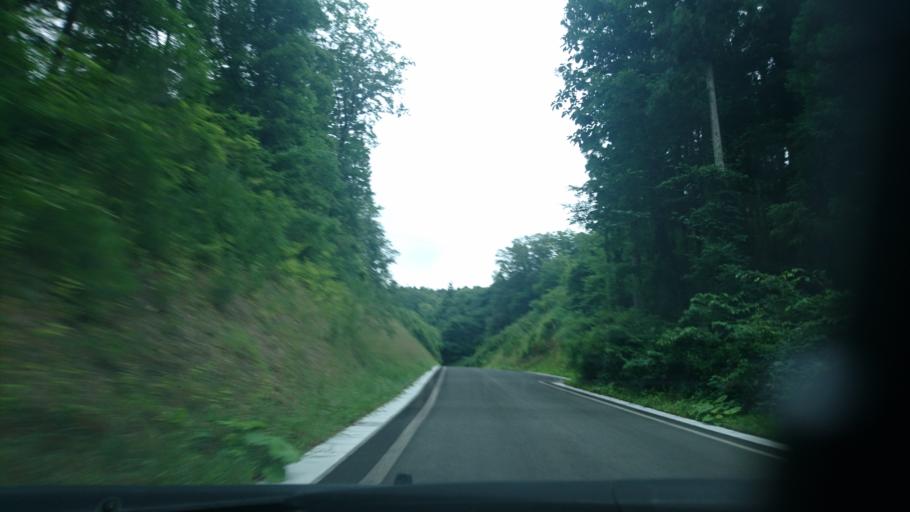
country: JP
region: Iwate
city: Ichinoseki
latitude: 38.9057
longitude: 141.2946
